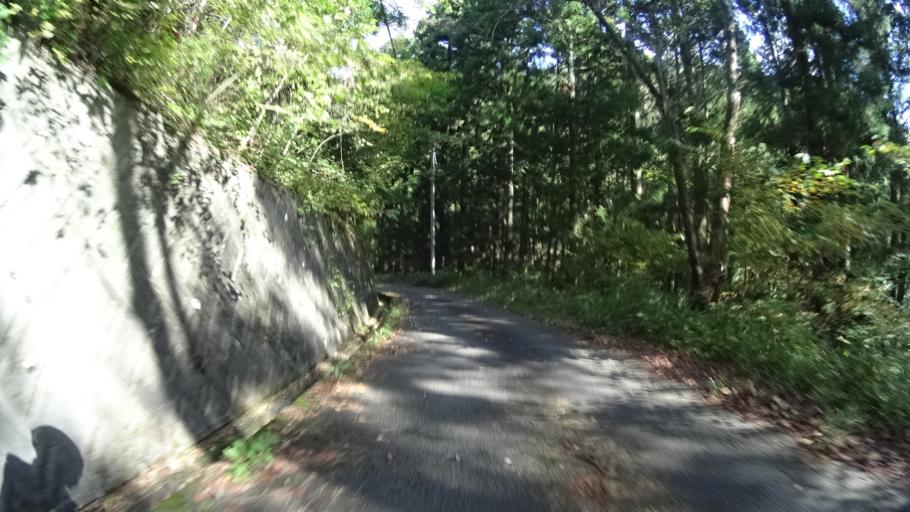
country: JP
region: Yamanashi
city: Otsuki
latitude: 35.5760
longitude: 138.9866
